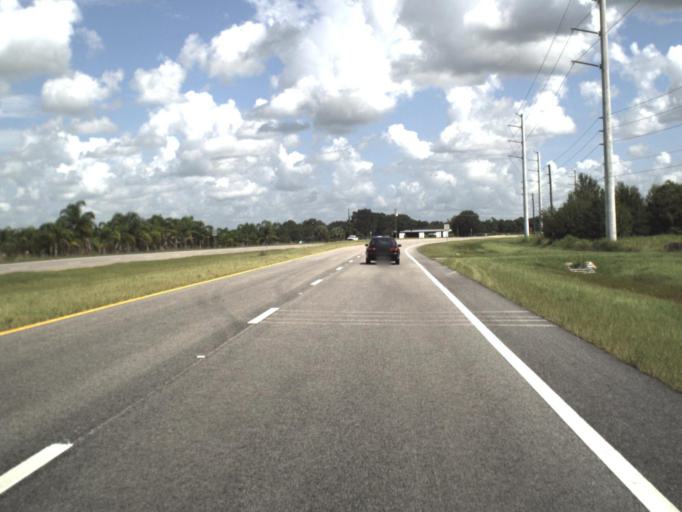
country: US
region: Florida
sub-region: Charlotte County
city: Harbour Heights
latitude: 27.0756
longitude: -81.9581
